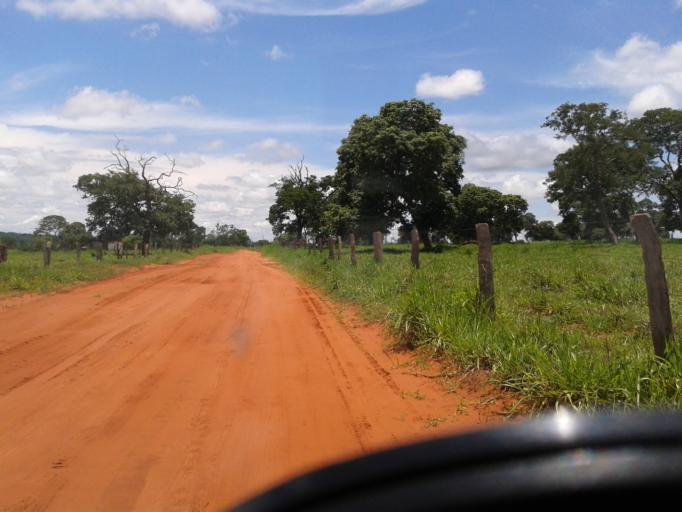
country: BR
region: Minas Gerais
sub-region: Santa Vitoria
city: Santa Vitoria
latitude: -18.9546
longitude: -49.8637
